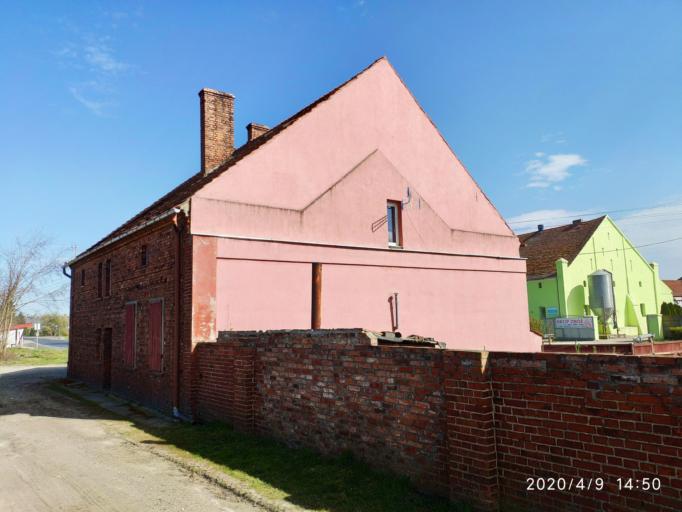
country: PL
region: Lubusz
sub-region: Powiat zielonogorski
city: Trzebiechow
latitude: 52.1174
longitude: 15.7191
